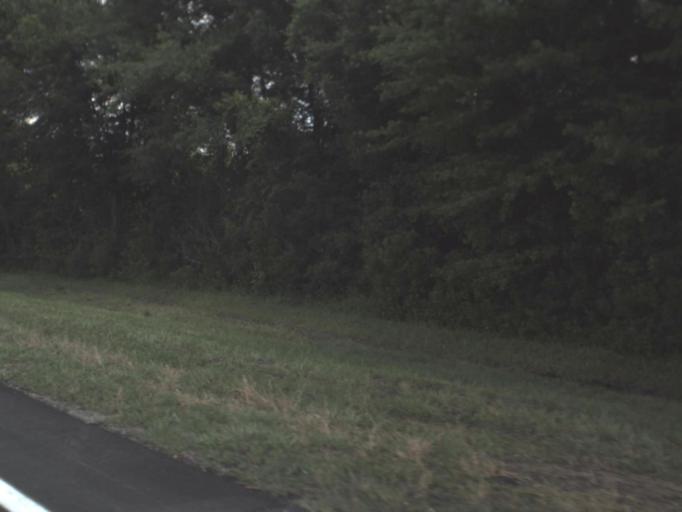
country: US
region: Florida
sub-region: Alachua County
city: Alachua
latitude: 29.7598
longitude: -82.4024
